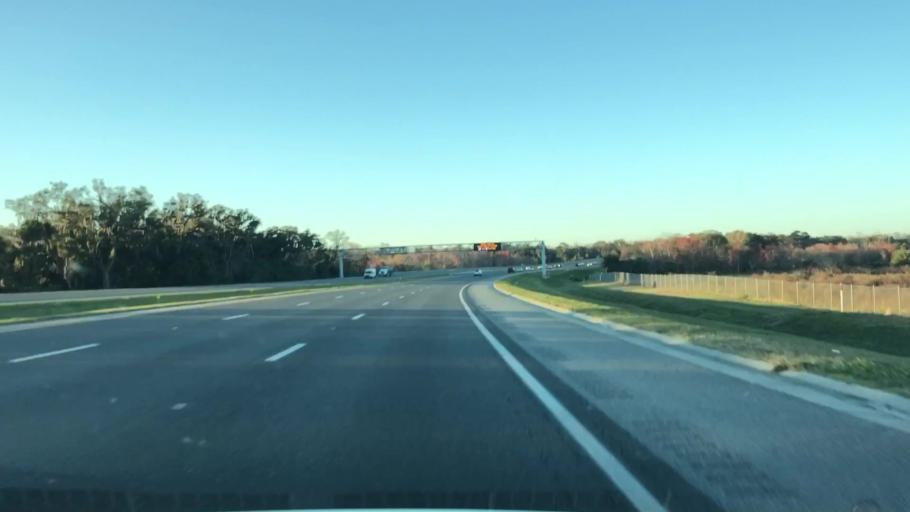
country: US
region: Florida
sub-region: Orange County
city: Apopka
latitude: 28.6732
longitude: -81.5577
